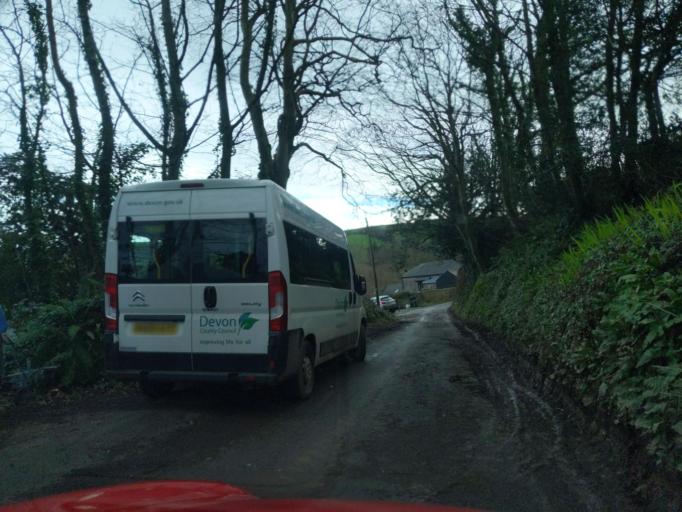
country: GB
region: England
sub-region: Devon
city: Salcombe
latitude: 50.2557
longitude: -3.6698
